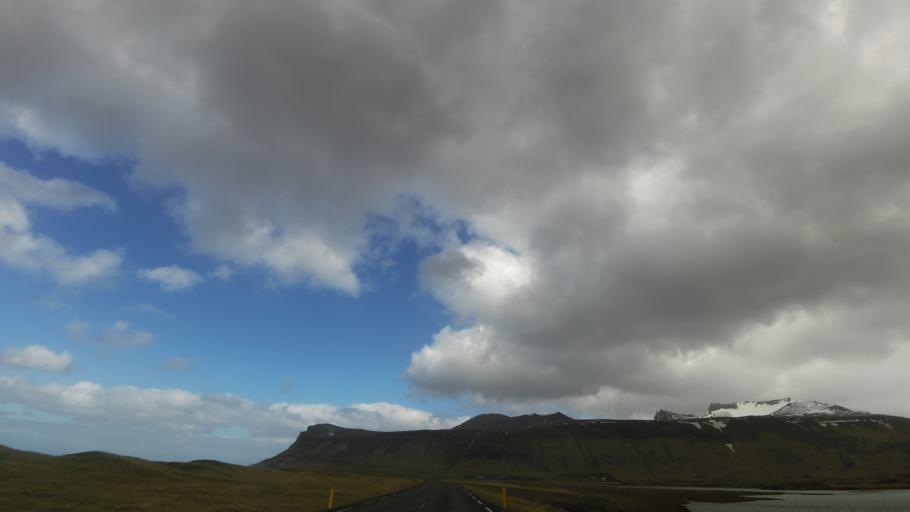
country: IS
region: West
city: Olafsvik
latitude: 64.9199
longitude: -23.5268
